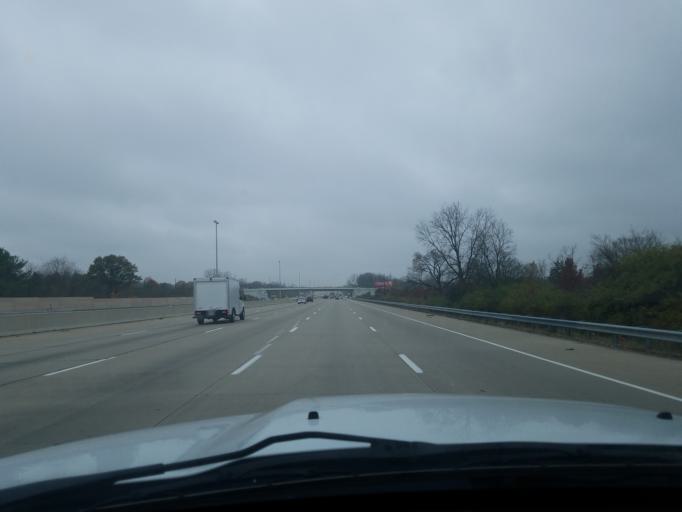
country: US
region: Indiana
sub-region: Marion County
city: Meridian Hills
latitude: 39.9248
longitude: -86.1230
